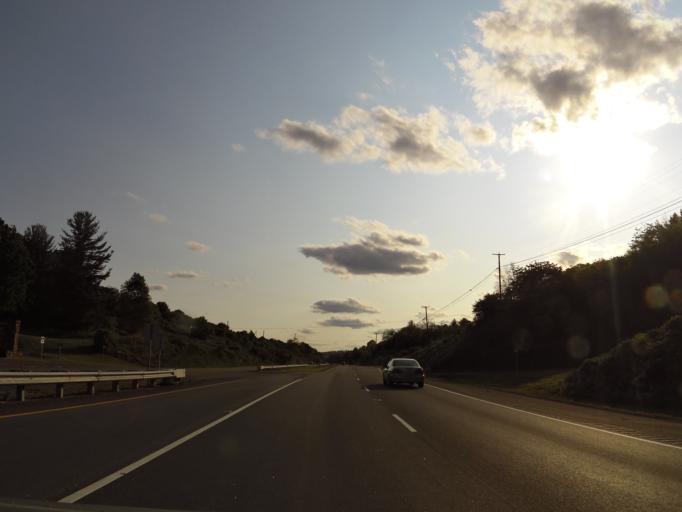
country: US
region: Virginia
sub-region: Tazewell County
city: Claypool Hill
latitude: 37.0083
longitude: -81.7960
